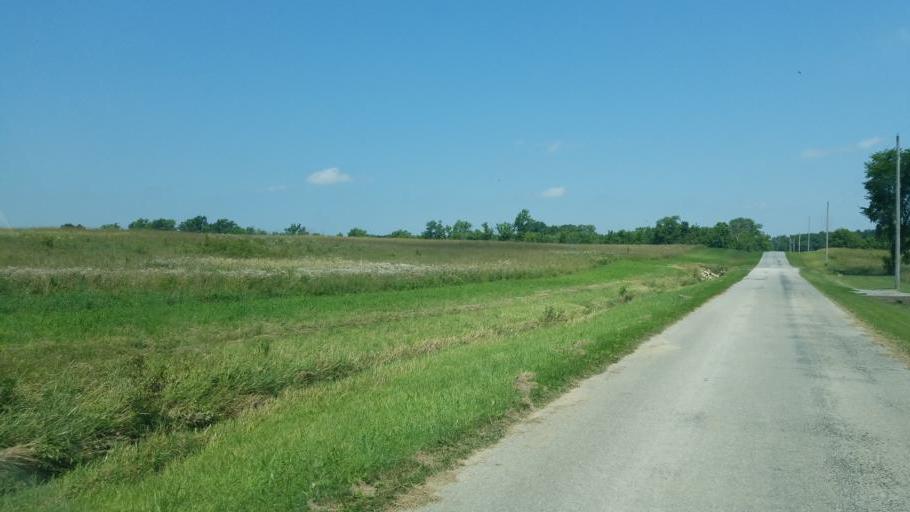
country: US
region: Ohio
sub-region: Sandusky County
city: Green Springs
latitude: 41.1114
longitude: -82.9766
